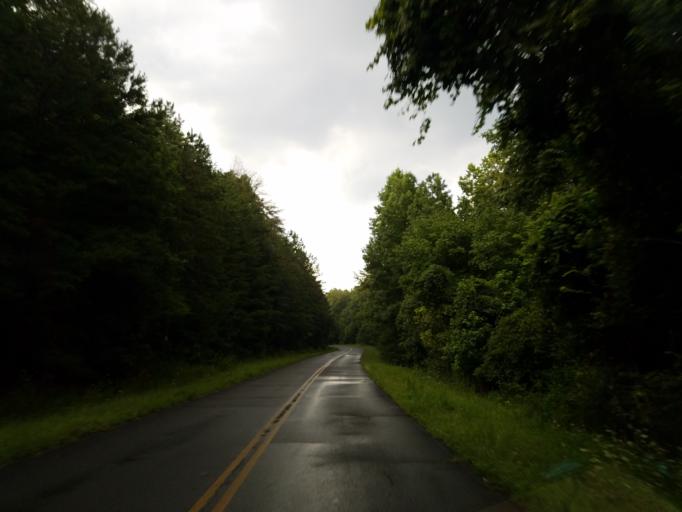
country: US
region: Georgia
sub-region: Whitfield County
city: Dalton
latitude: 34.6456
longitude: -85.0896
